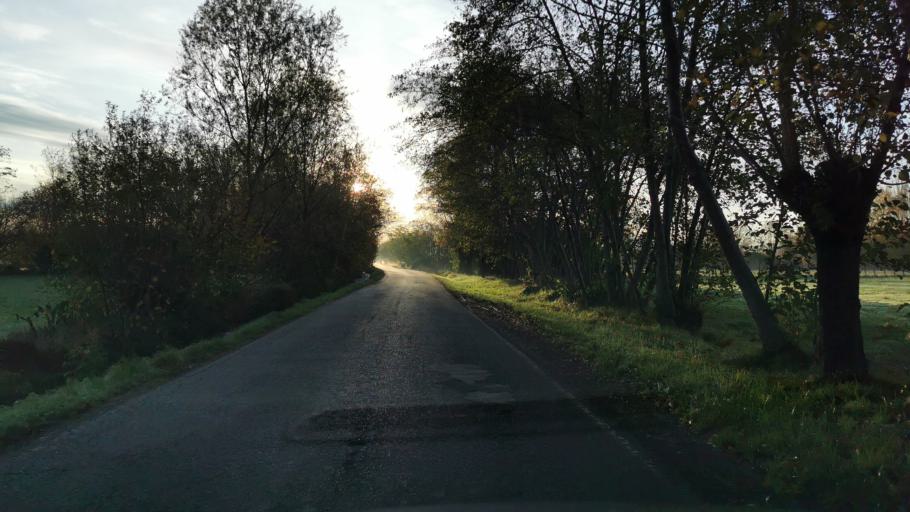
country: IT
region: Piedmont
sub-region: Provincia di Torino
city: San Francesco al Campo
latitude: 45.2070
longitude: 7.6622
